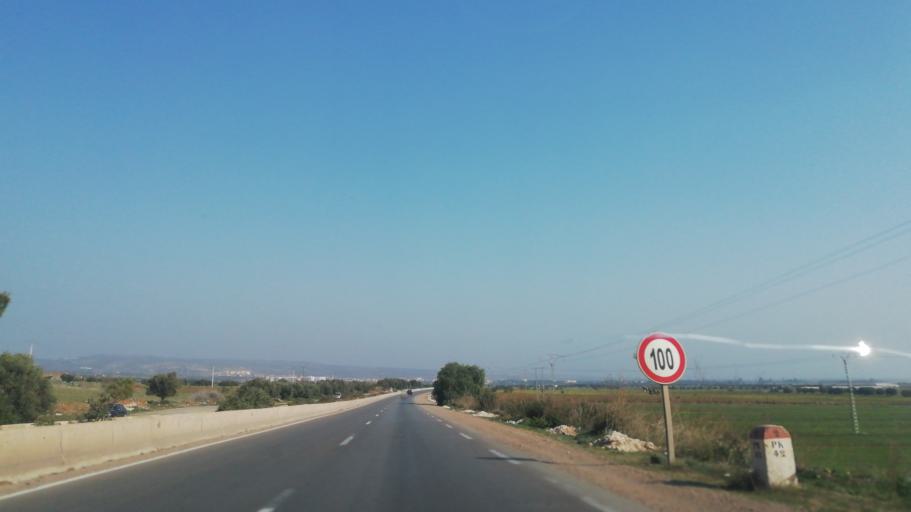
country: DZ
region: Oran
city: Bou Tlelis
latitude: 35.5594
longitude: -0.9320
